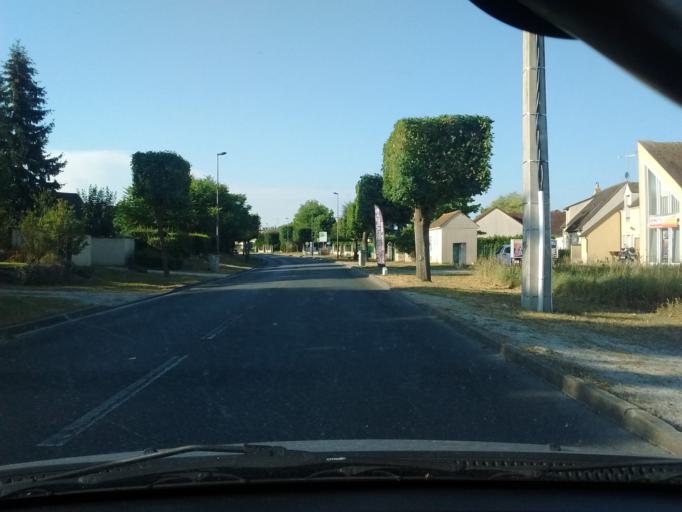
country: FR
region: Ile-de-France
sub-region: Departement de l'Essonne
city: Milly-la-Foret
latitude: 48.4107
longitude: 2.4661
